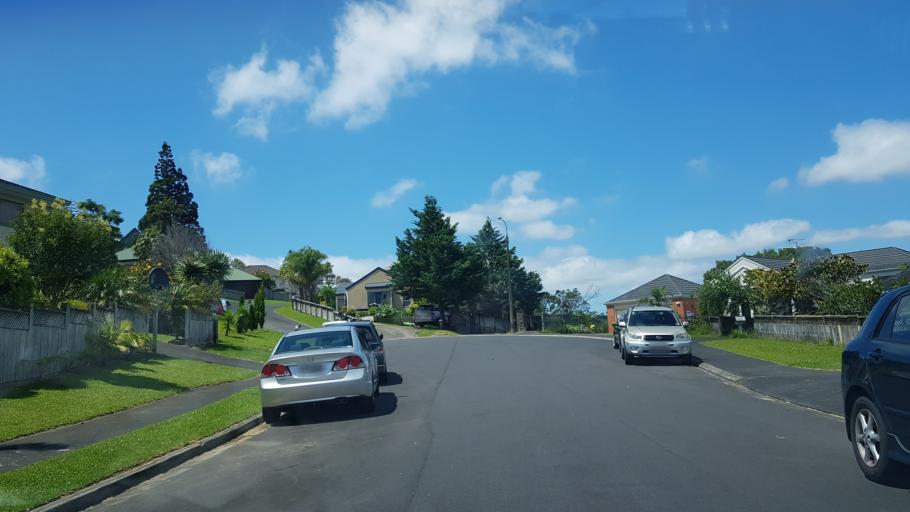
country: NZ
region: Auckland
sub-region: Auckland
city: North Shore
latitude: -36.7884
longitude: 174.7067
